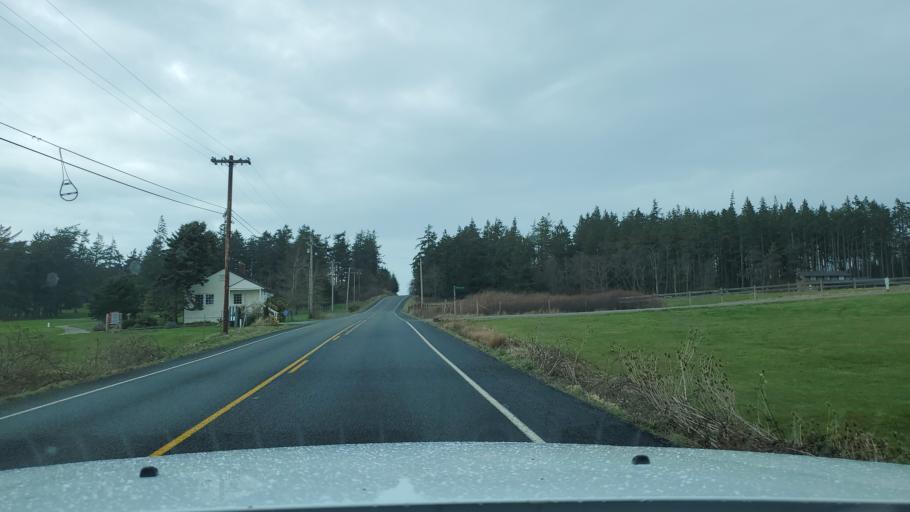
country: US
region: Washington
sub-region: Island County
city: Ault Field
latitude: 48.3201
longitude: -122.6912
